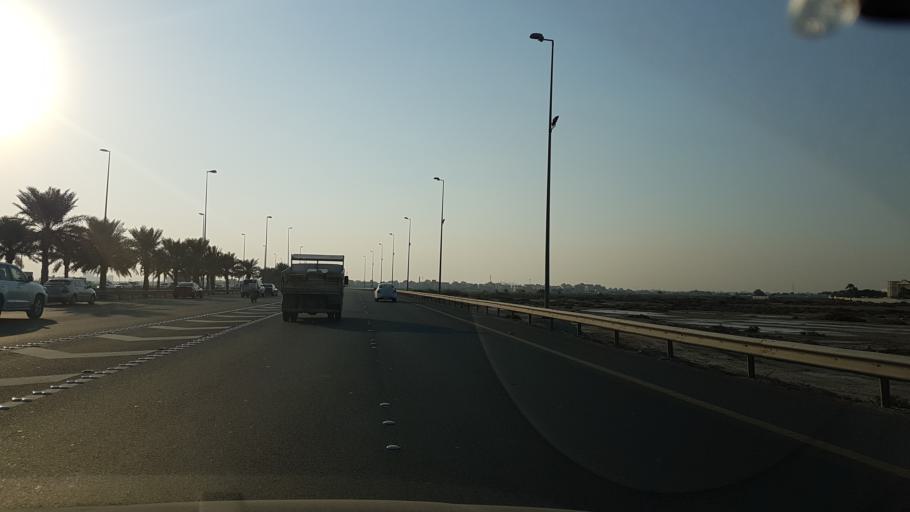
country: BH
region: Northern
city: Madinat `Isa
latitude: 26.1959
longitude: 50.5285
